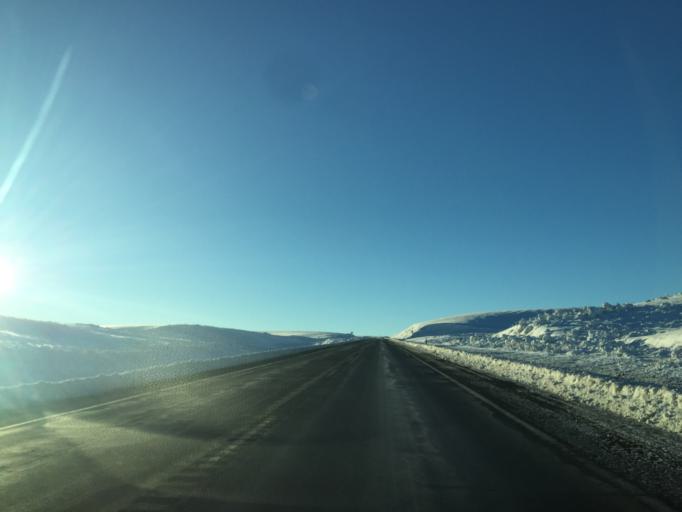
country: US
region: Washington
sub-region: Grant County
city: Soap Lake
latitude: 47.6212
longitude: -119.4025
